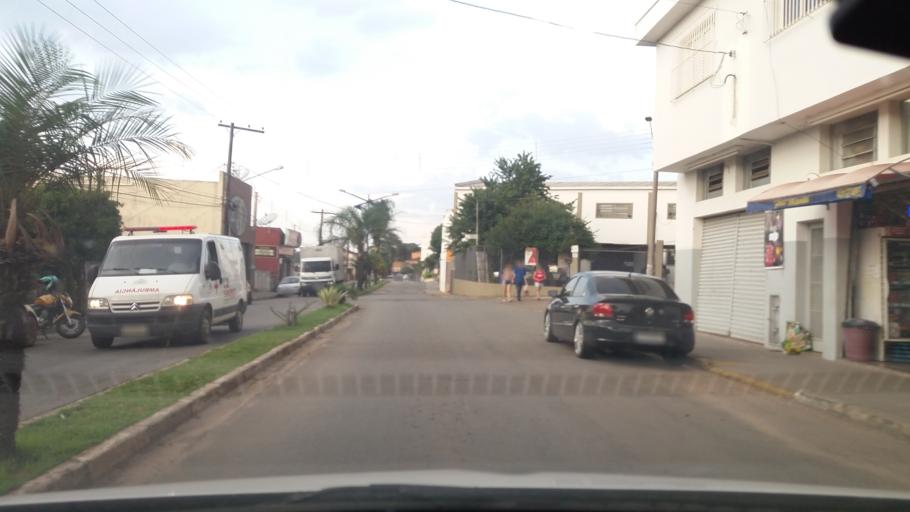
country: BR
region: Sao Paulo
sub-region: Bom Jesus Dos Perdoes
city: Bom Jesus dos Perdoes
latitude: -23.1384
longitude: -46.4665
